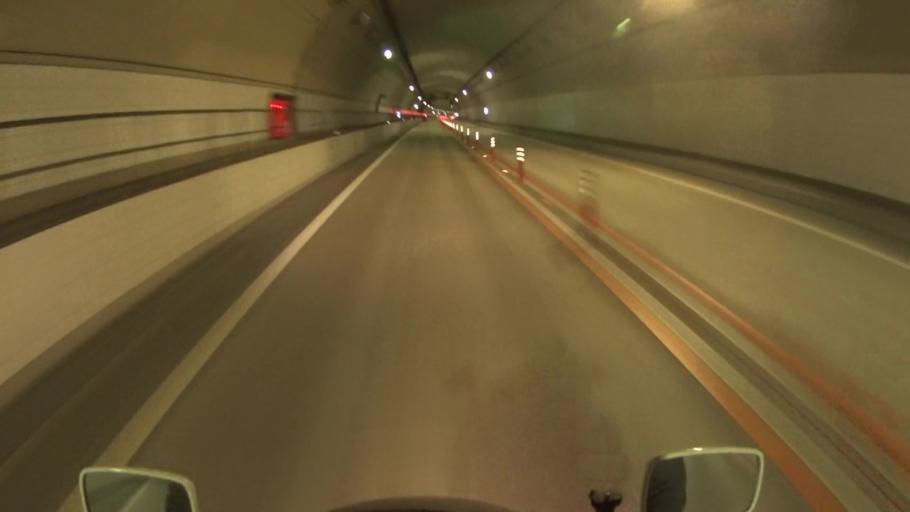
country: JP
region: Kyoto
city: Miyazu
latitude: 35.5409
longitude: 135.1569
